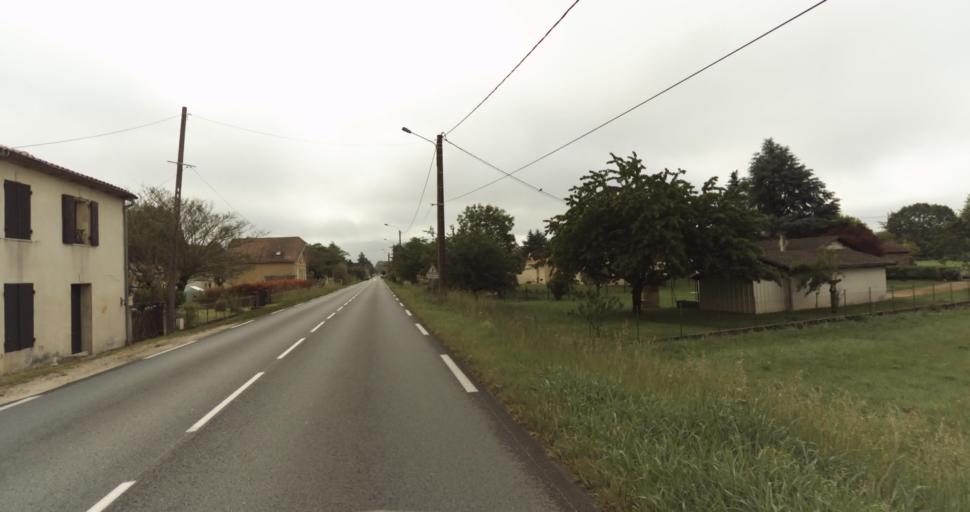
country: FR
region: Aquitaine
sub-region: Departement de la Dordogne
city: Mouleydier
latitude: 44.8501
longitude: 0.6220
